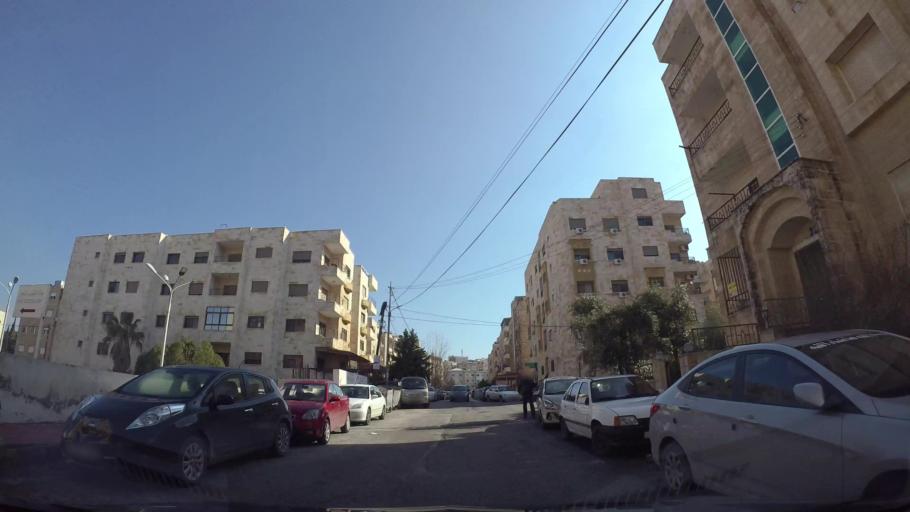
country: JO
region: Amman
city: Al Jubayhah
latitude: 32.0043
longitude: 35.8777
